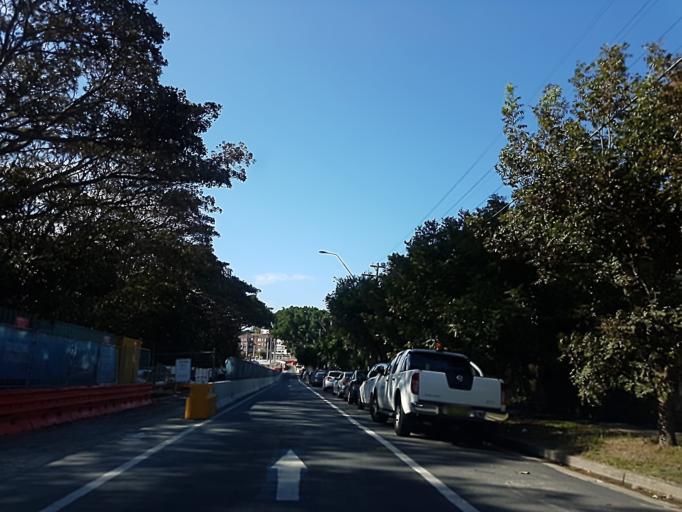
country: AU
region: New South Wales
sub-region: Randwick
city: Kingsford
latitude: -33.9137
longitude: 151.2353
